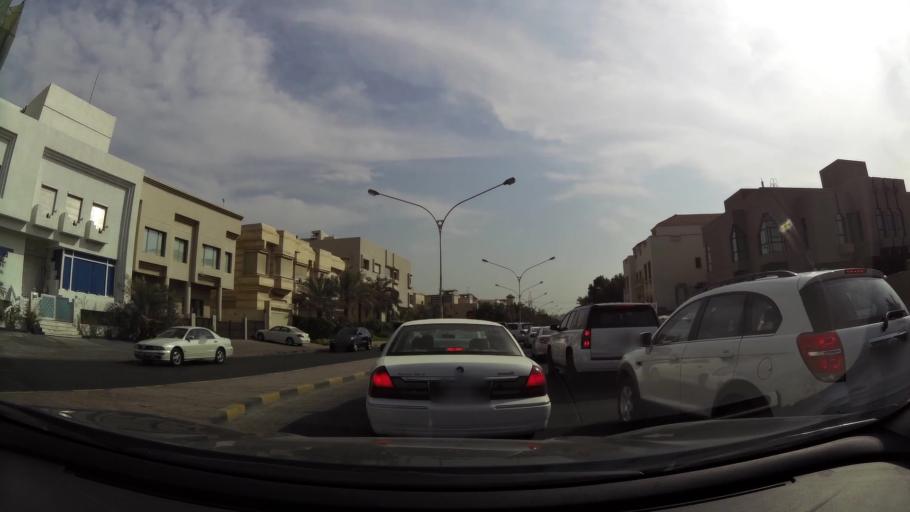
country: KW
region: Al Farwaniyah
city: Al Farwaniyah
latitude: 29.3083
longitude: 47.9709
